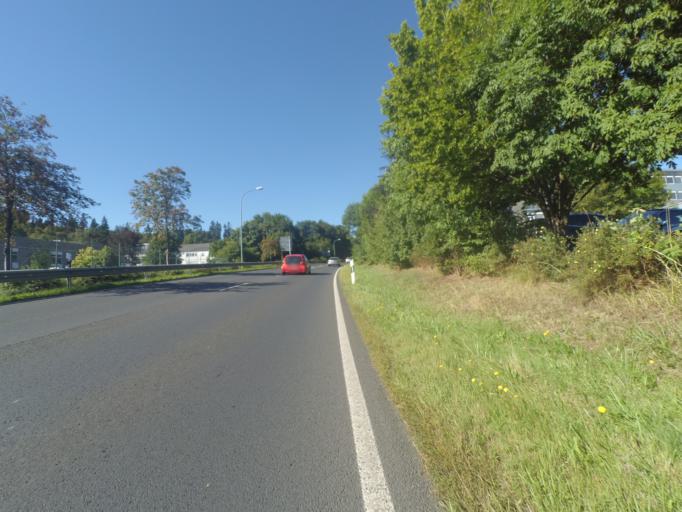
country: DE
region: Rheinland-Pfalz
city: Daun
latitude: 50.1990
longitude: 6.8220
